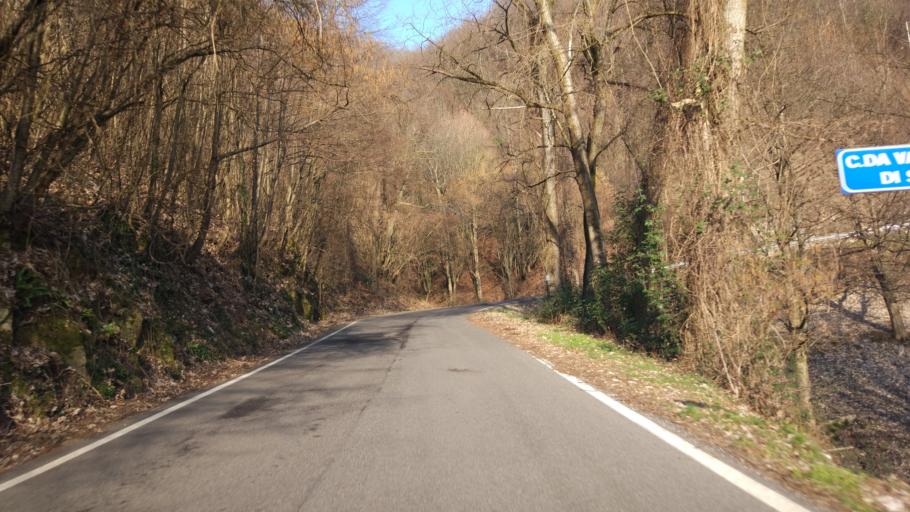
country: IT
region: Veneto
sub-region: Provincia di Verona
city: Selva di Progno
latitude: 45.6065
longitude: 11.1663
